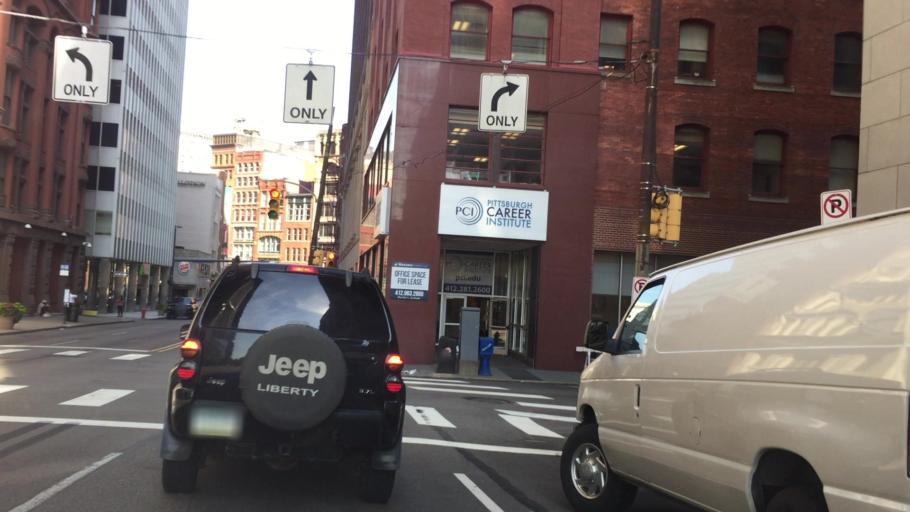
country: US
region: Pennsylvania
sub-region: Allegheny County
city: Pittsburgh
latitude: 40.4424
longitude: -79.9955
